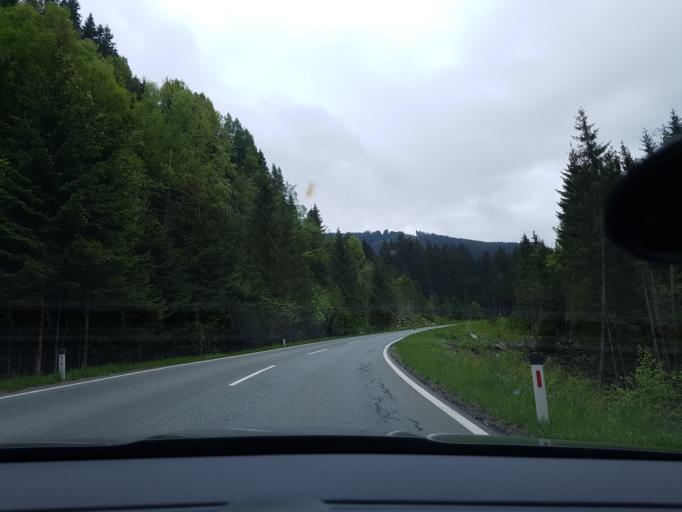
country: AT
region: Salzburg
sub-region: Politischer Bezirk Zell am See
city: Krimml
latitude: 47.2142
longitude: 12.1657
